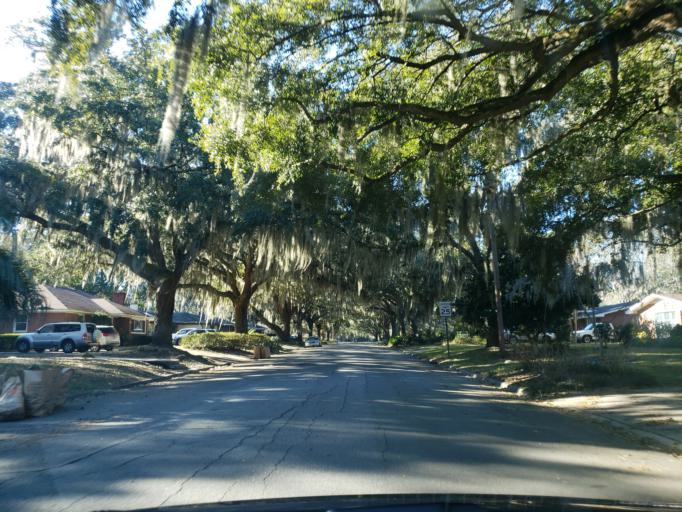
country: US
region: Georgia
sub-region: Chatham County
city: Thunderbolt
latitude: 32.0206
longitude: -81.0997
